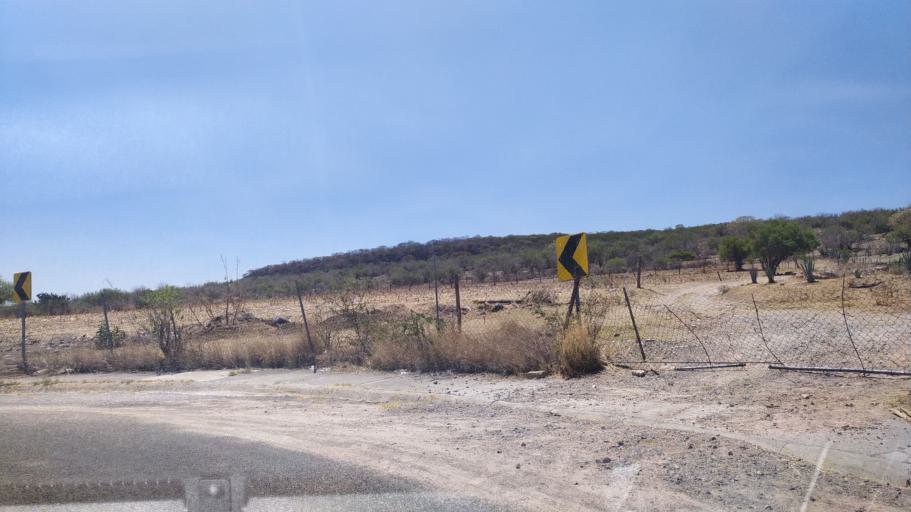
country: MX
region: Guanajuato
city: Ciudad Manuel Doblado
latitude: 20.7557
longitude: -101.9685
